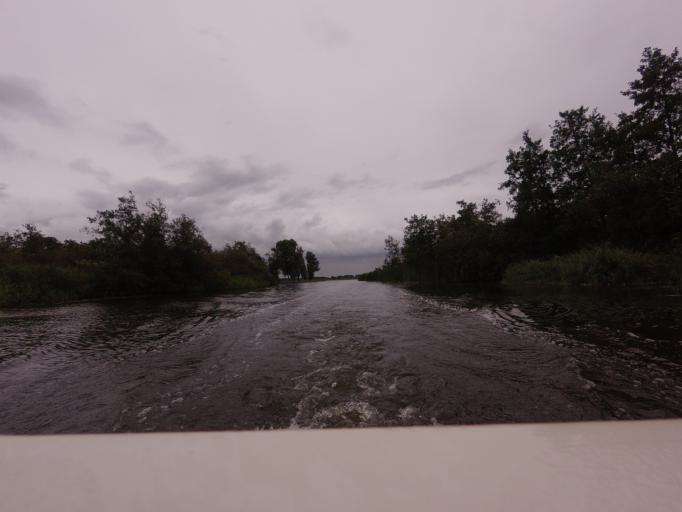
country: NL
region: Friesland
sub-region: Gemeente Boarnsterhim
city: Warten
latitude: 53.1176
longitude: 5.9328
